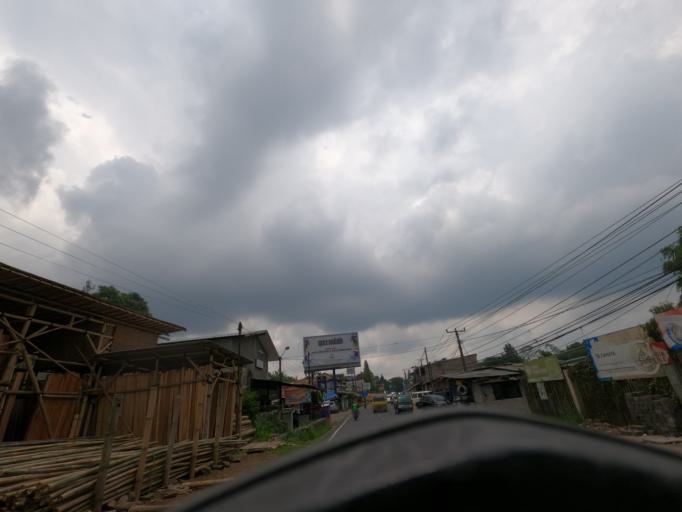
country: ID
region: West Java
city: Sukabumi
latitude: -6.7554
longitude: 107.0464
